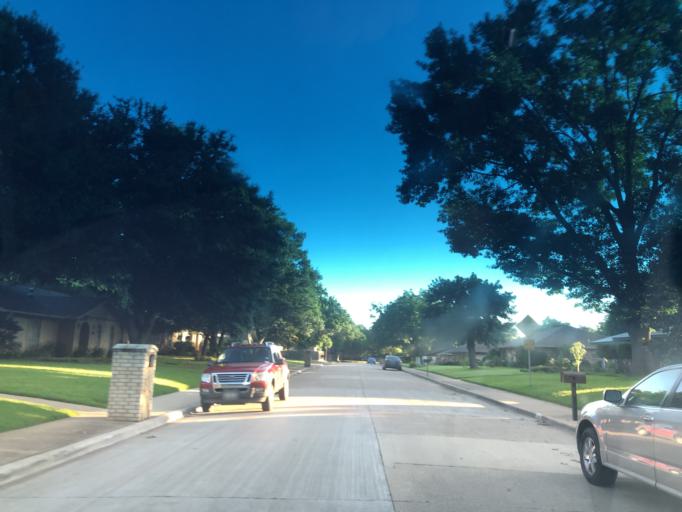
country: US
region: Texas
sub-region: Dallas County
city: Grand Prairie
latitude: 32.7803
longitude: -97.0329
